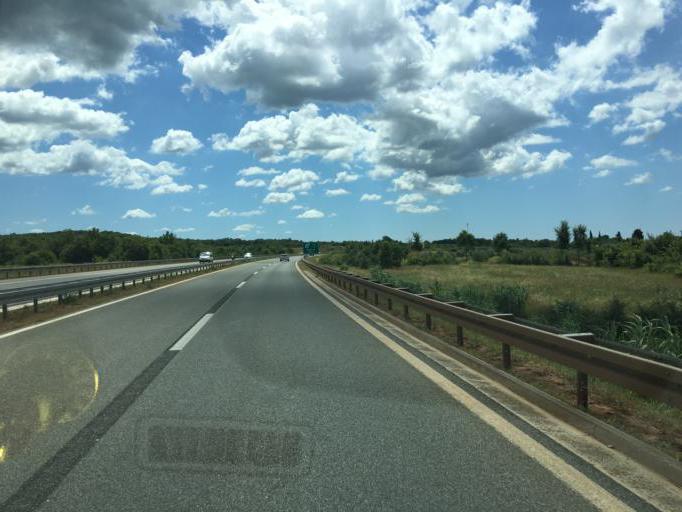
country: HR
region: Istarska
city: Karojba
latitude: 45.2360
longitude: 13.7195
